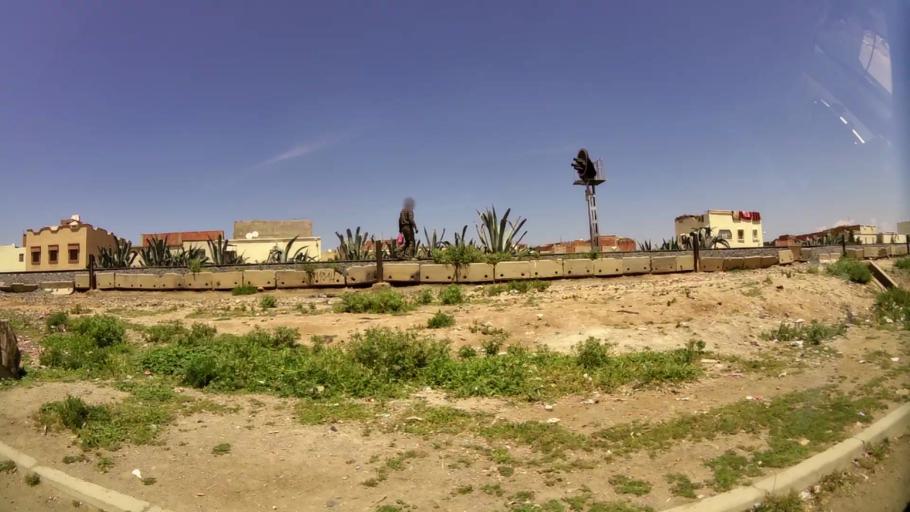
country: MA
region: Oriental
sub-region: Oujda-Angad
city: Oujda
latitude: 34.6948
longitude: -1.9468
